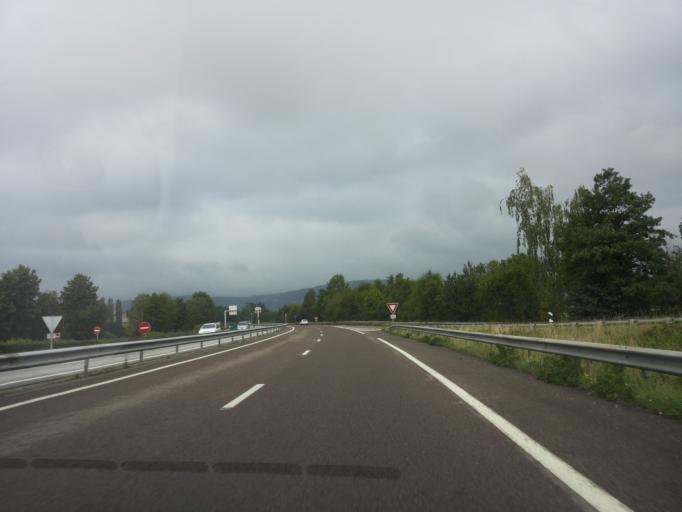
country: FR
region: Lorraine
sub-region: Departement des Vosges
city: Saint-Etienne-les-Remiremont
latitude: 48.0154
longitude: 6.6090
